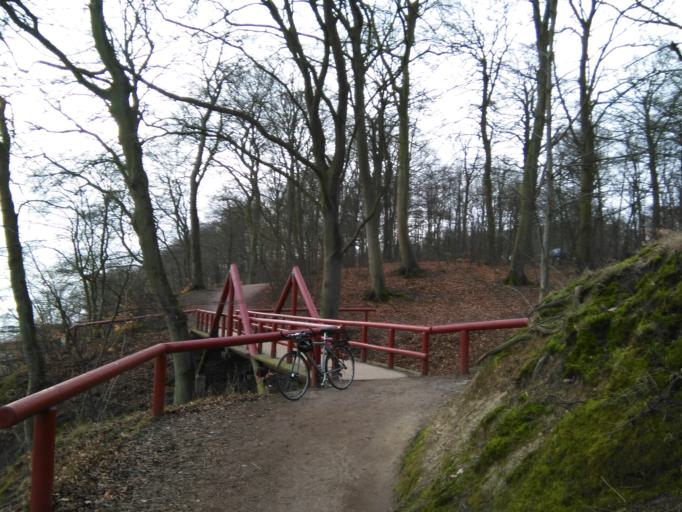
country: DK
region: Central Jutland
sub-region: Arhus Kommune
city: Arhus
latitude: 56.1217
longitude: 10.2231
